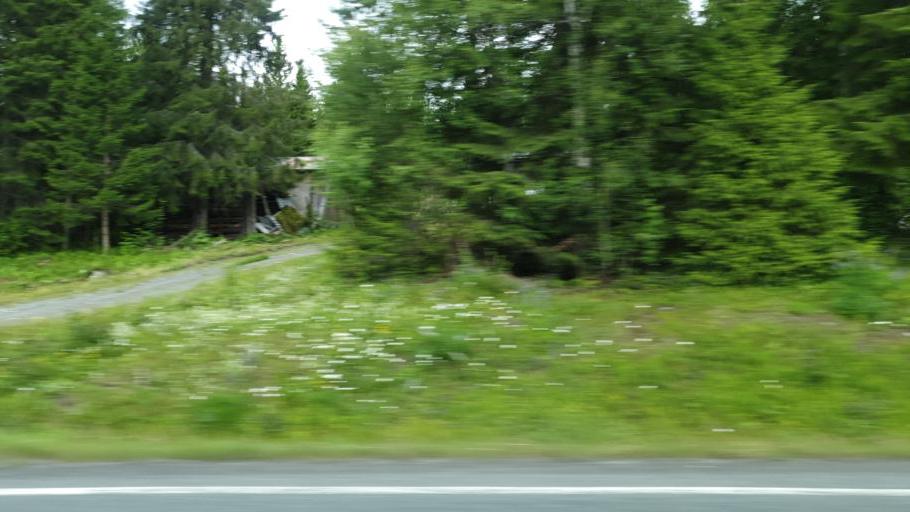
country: NO
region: Sor-Trondelag
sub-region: Rennebu
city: Berkak
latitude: 62.8475
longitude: 10.0181
